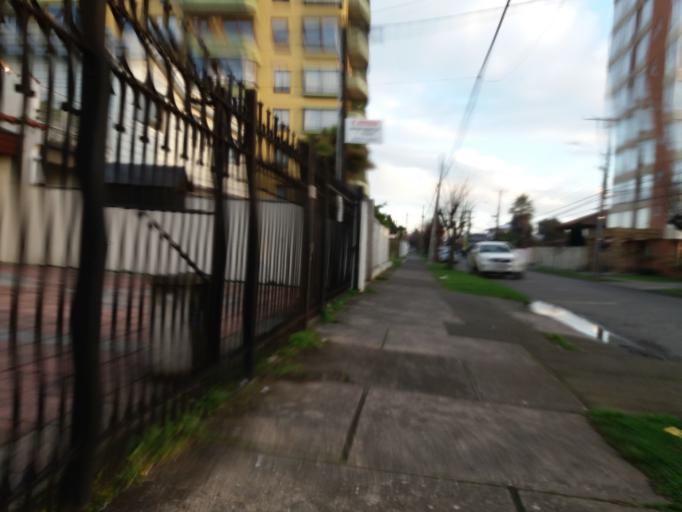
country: CL
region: Araucania
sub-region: Provincia de Cautin
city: Temuco
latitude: -38.7381
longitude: -72.6049
